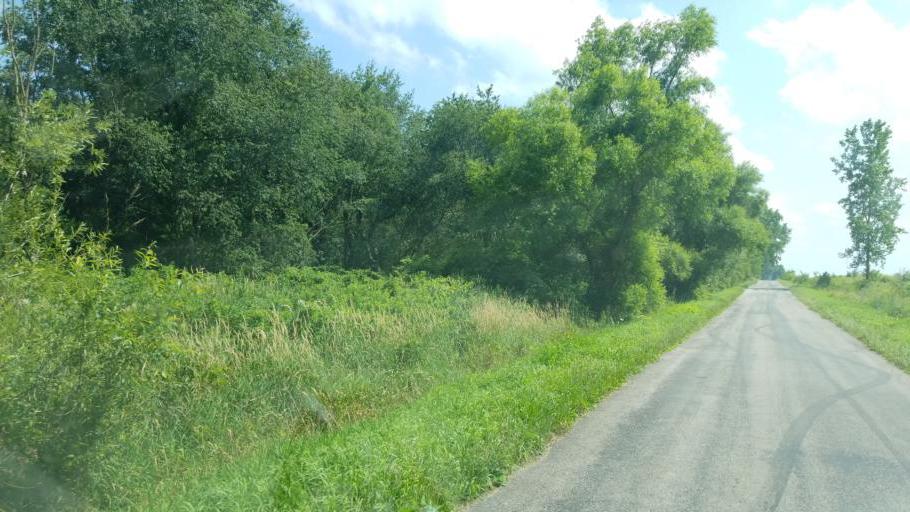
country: US
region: Ohio
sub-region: Huron County
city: Willard
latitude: 41.0158
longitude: -82.7810
